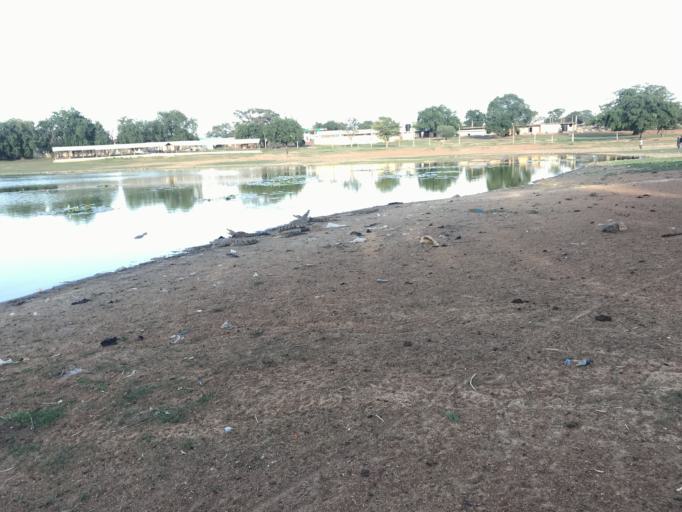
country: GH
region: Upper East
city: Navrongo
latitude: 10.9846
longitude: -1.1095
